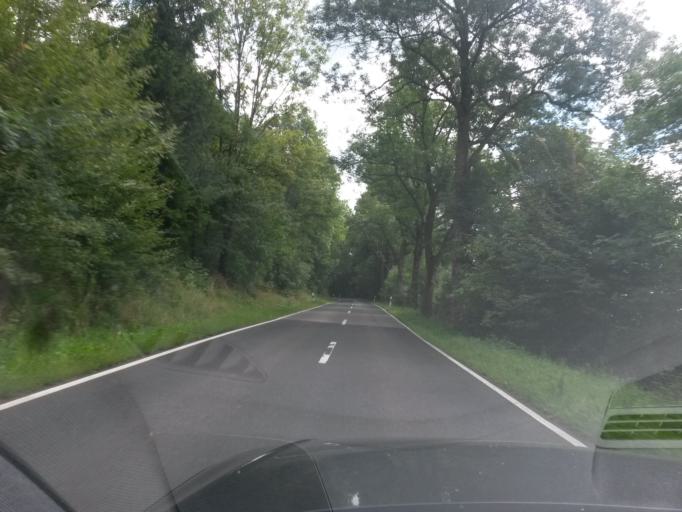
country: DE
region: Hesse
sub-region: Regierungsbezirk Kassel
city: Hilders
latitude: 50.5649
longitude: 10.0193
